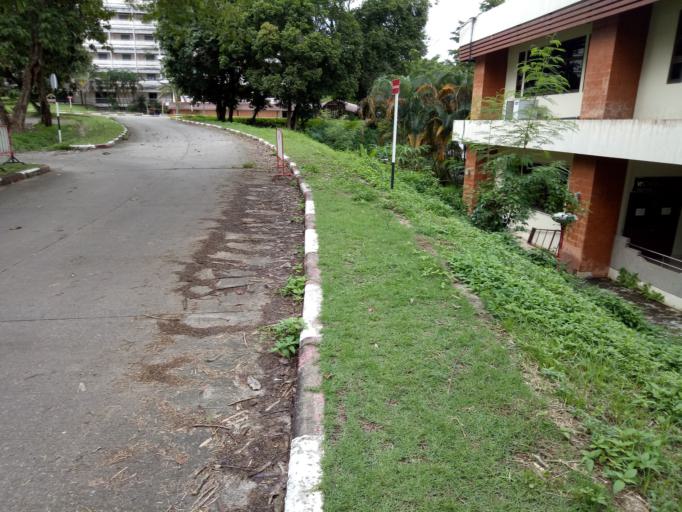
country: TH
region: Chiang Rai
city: Chiang Rai
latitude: 19.9838
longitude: 99.8460
